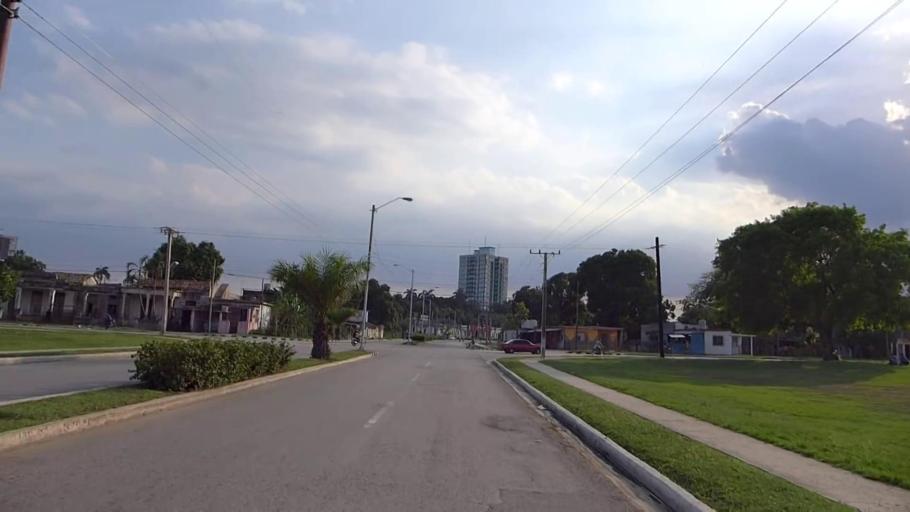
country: CU
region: Camaguey
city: Camaguey
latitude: 21.3818
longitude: -77.9088
